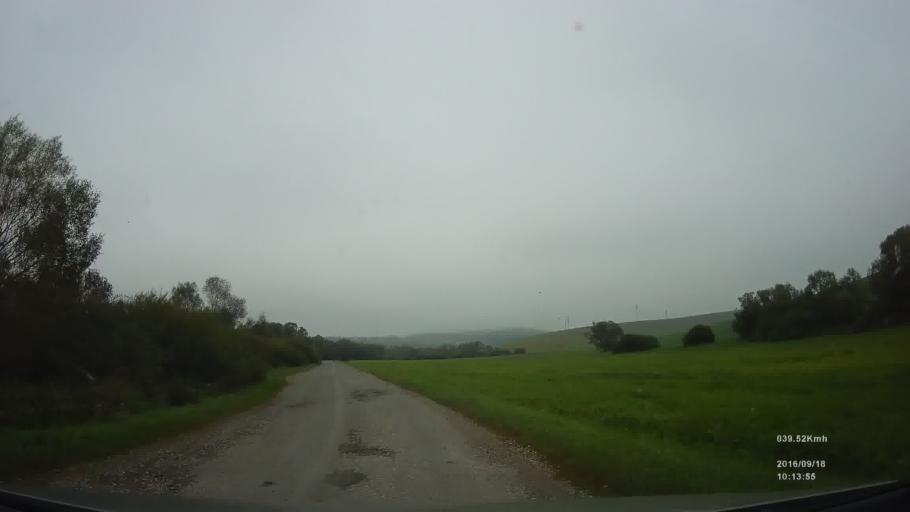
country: SK
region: Kosicky
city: Spisska Nova Ves
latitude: 48.9377
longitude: 20.6304
